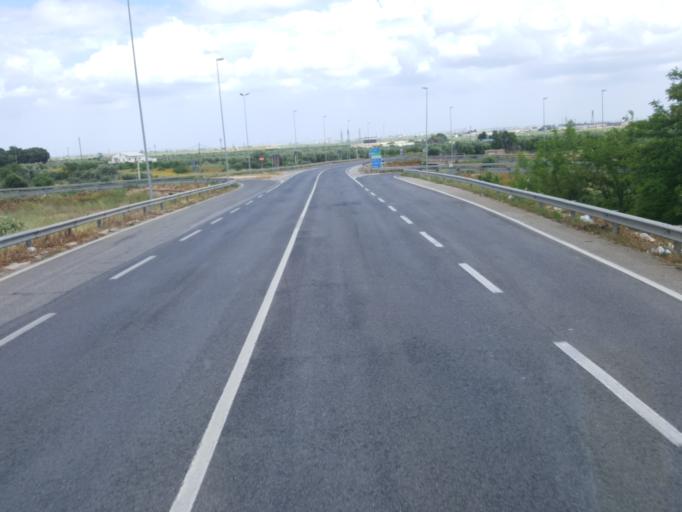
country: IT
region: Apulia
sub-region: Provincia di Bari
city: Palo del Colle
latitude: 41.0551
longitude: 16.7116
